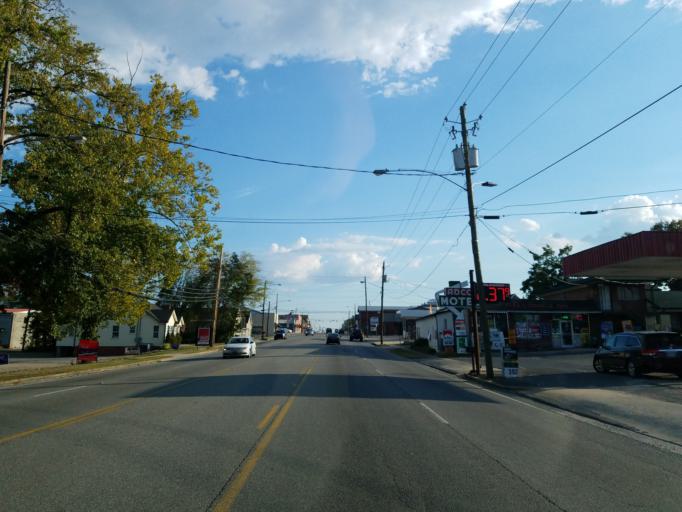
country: US
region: Georgia
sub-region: Murray County
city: Chatsworth
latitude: 34.7700
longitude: -84.7696
